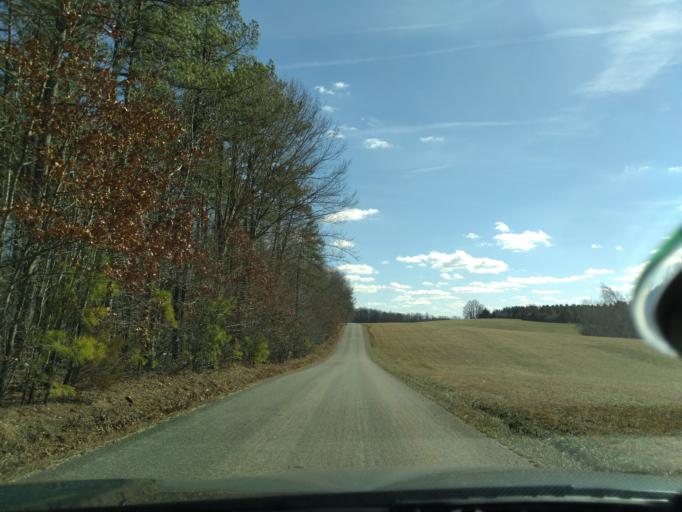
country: US
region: Virginia
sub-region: Nottoway County
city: Crewe
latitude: 37.1751
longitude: -78.2631
